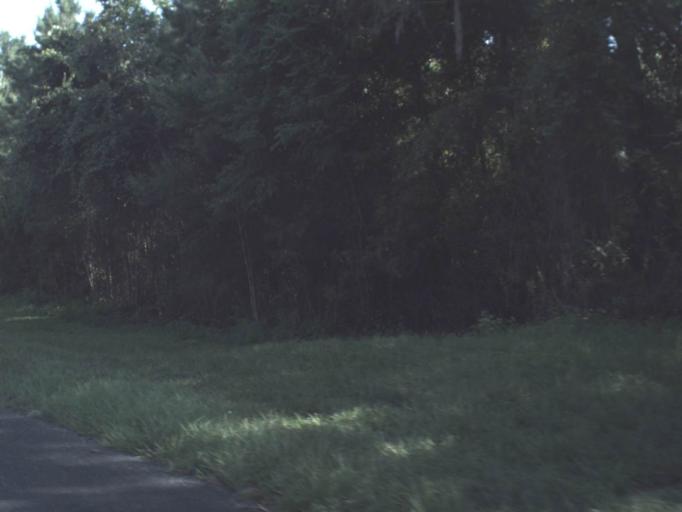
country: US
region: Florida
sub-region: Taylor County
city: Perry
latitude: 30.2921
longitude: -83.6331
